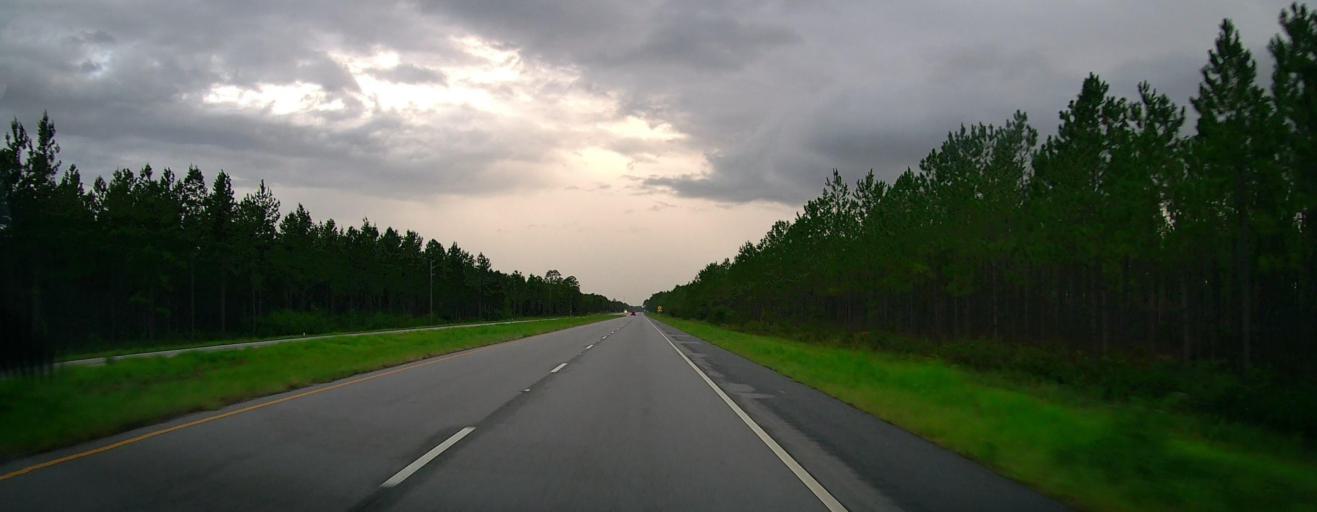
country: US
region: Georgia
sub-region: Ware County
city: Deenwood
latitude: 31.1294
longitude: -82.5157
